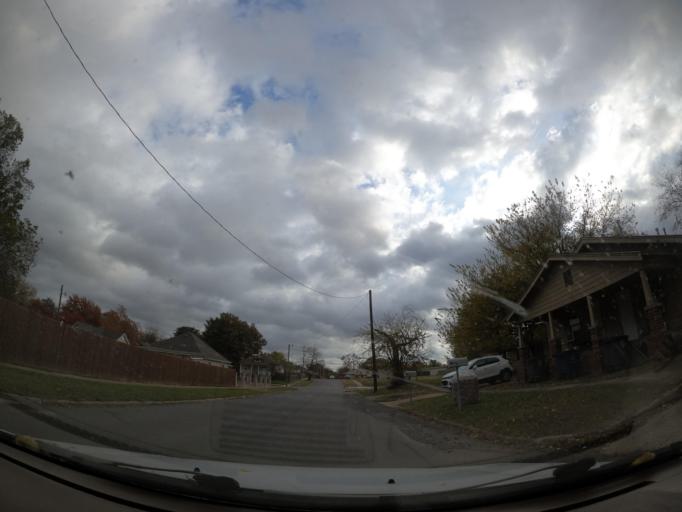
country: US
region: Oklahoma
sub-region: Tulsa County
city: Tulsa
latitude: 36.1638
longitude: -95.9601
